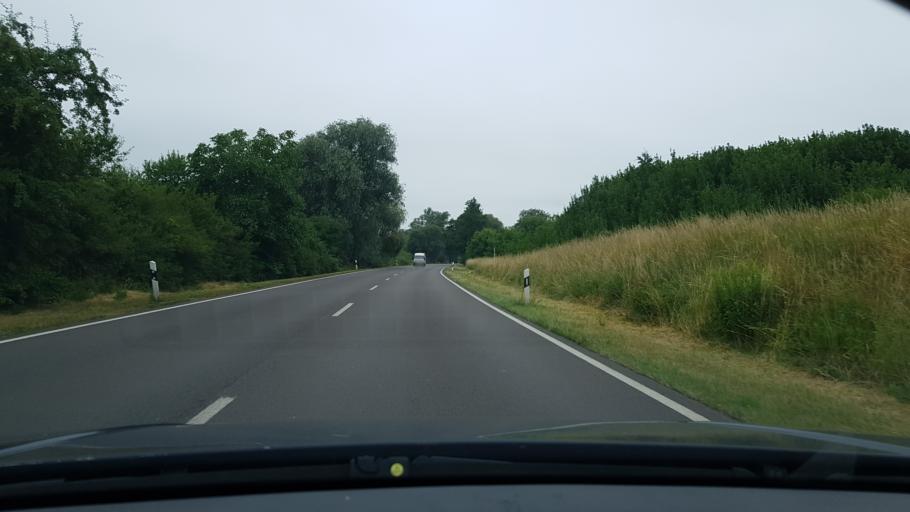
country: DE
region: Brandenburg
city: Angermunde
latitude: 53.0120
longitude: 14.0089
